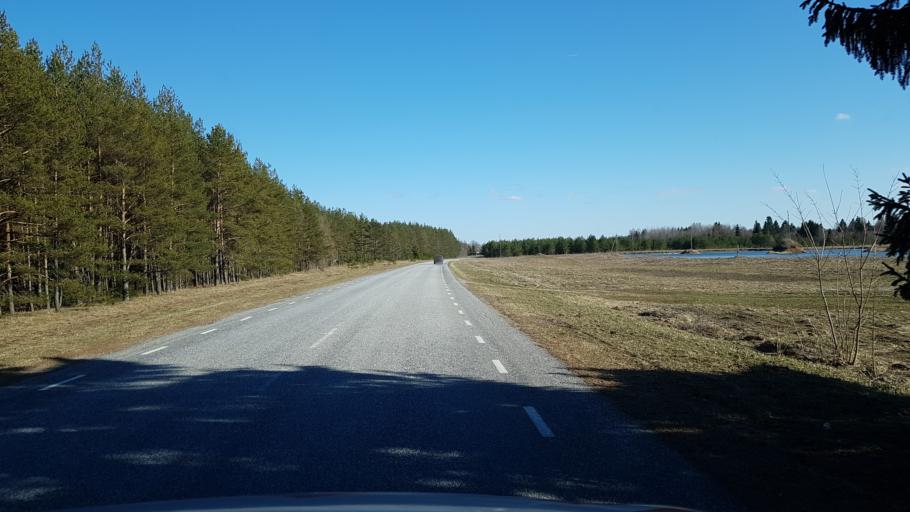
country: EE
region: Laeaene-Virumaa
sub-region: Haljala vald
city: Haljala
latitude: 59.4696
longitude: 26.1766
